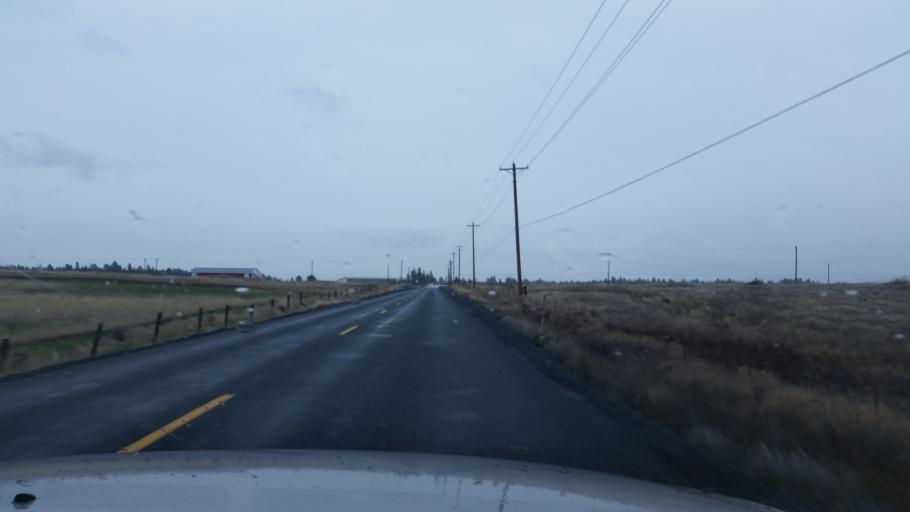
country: US
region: Washington
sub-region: Spokane County
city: Airway Heights
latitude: 47.6719
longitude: -117.5658
